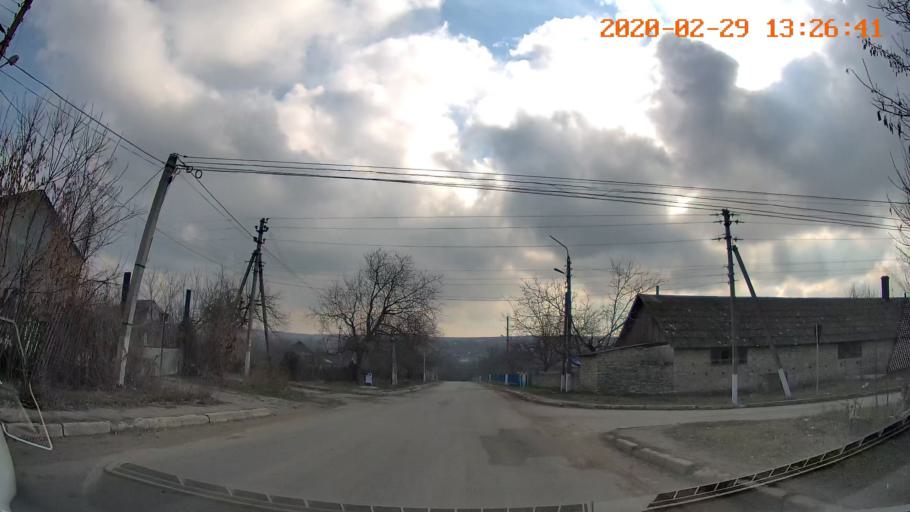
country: MD
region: Telenesti
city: Camenca
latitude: 47.9181
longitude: 28.6387
